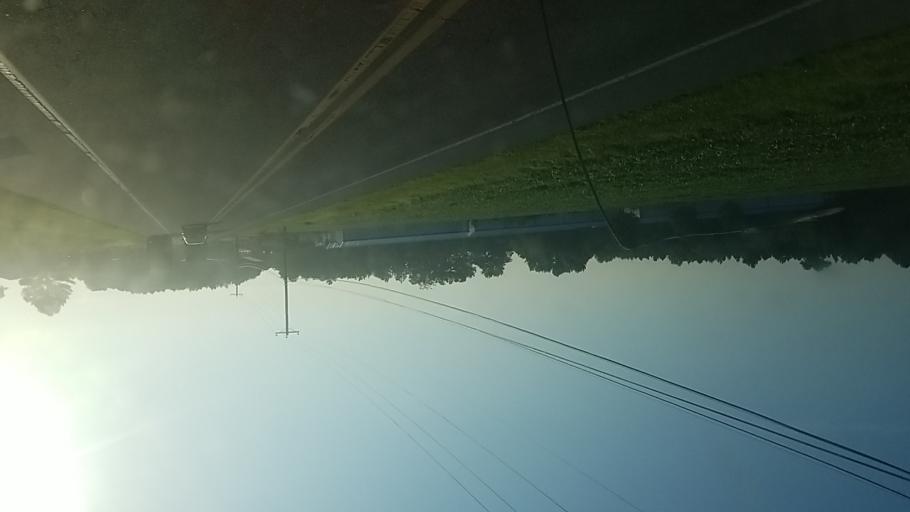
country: US
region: Delaware
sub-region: Sussex County
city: Selbyville
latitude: 38.4615
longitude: -75.1917
